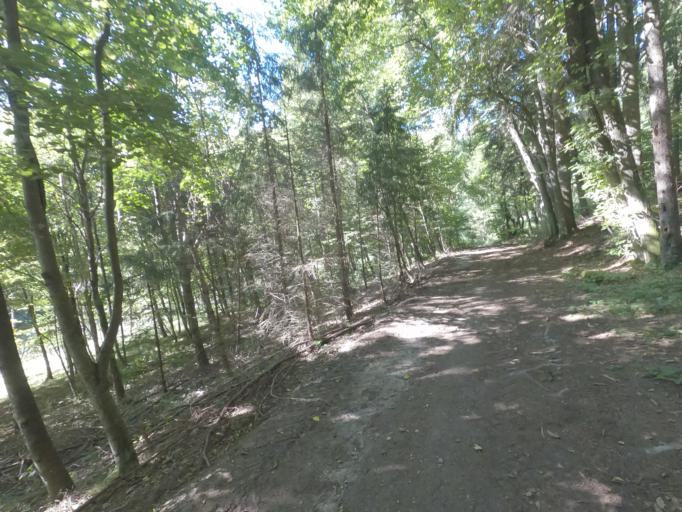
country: DE
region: Bavaria
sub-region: Lower Bavaria
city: Schaufling
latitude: 48.8326
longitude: 13.0174
